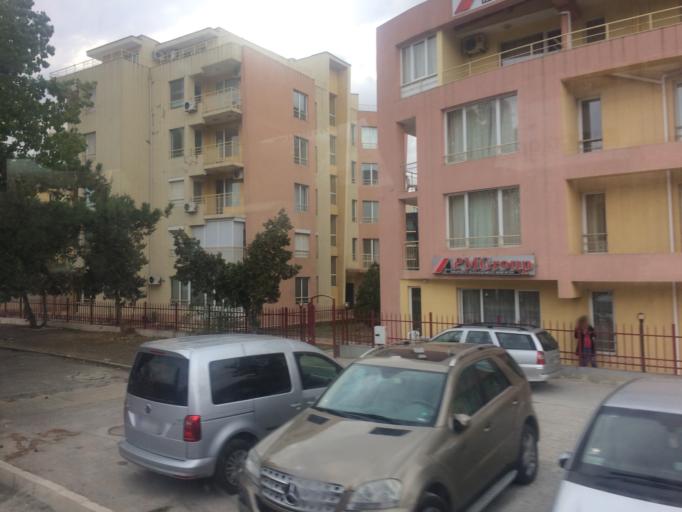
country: BG
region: Burgas
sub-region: Obshtina Nesebur
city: Sveti Vlas
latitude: 42.7047
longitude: 27.7171
